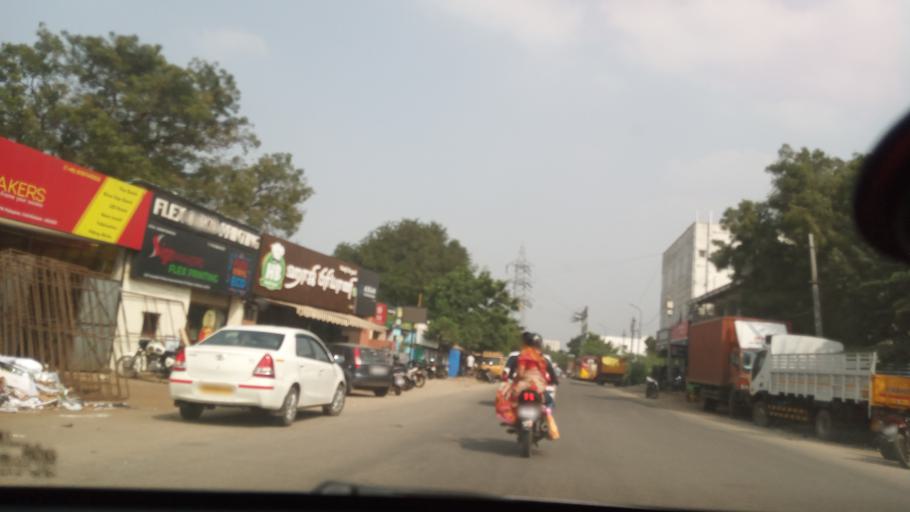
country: IN
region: Tamil Nadu
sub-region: Coimbatore
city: Coimbatore
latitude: 11.0213
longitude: 76.9826
